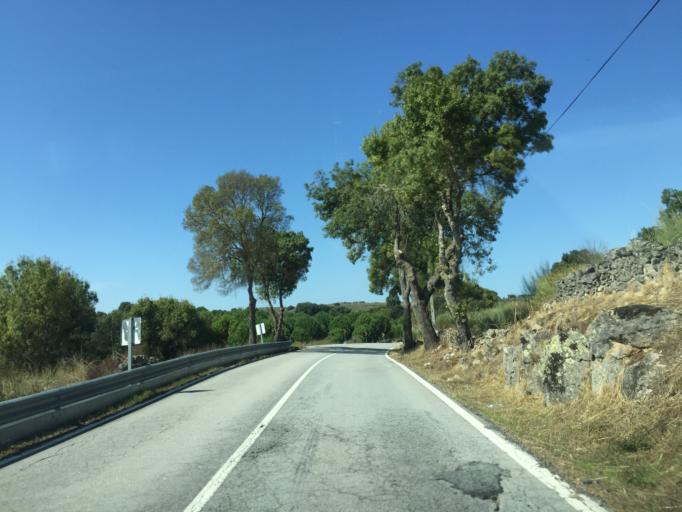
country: PT
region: Portalegre
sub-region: Portalegre
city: Alagoa
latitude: 39.4334
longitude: -7.5284
